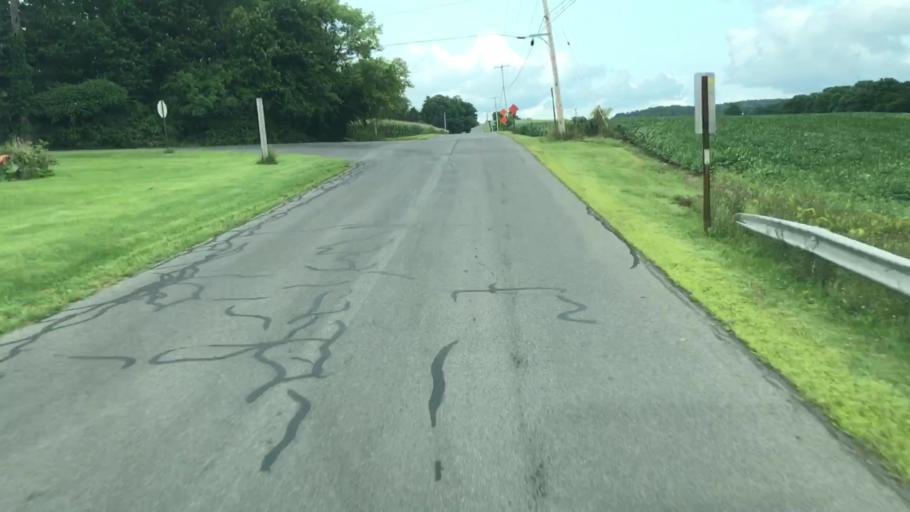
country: US
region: New York
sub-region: Onondaga County
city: Elbridge
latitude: 42.9849
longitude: -76.5071
